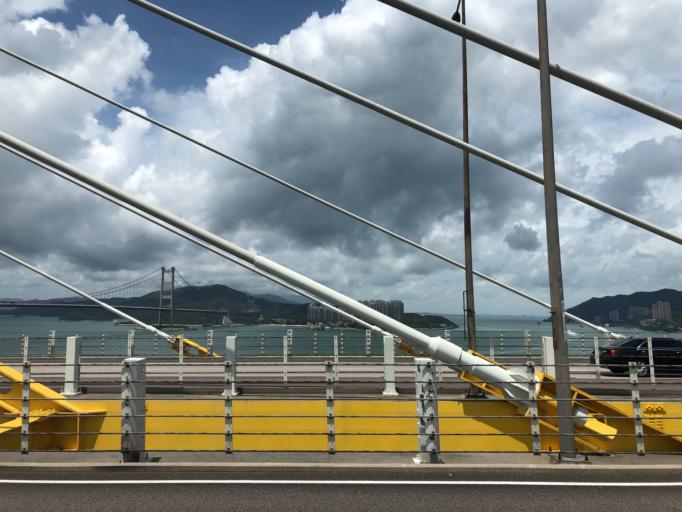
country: HK
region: Tsuen Wan
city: Tsuen Wan
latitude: 22.3619
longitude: 114.0809
